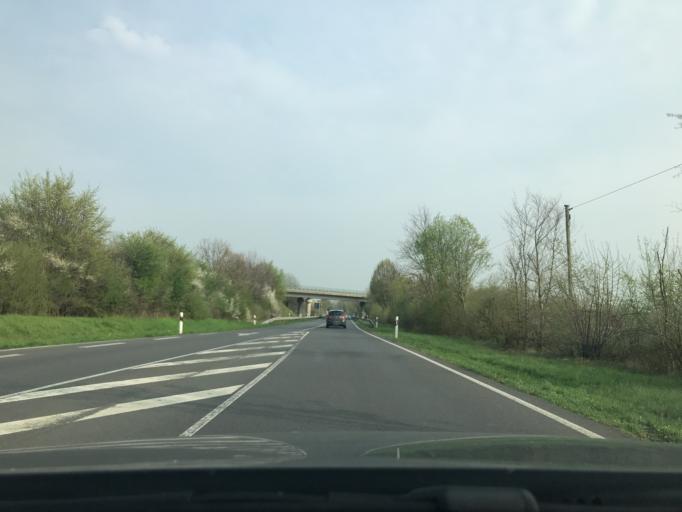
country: DE
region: North Rhine-Westphalia
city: Geldern
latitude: 51.4994
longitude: 6.3173
